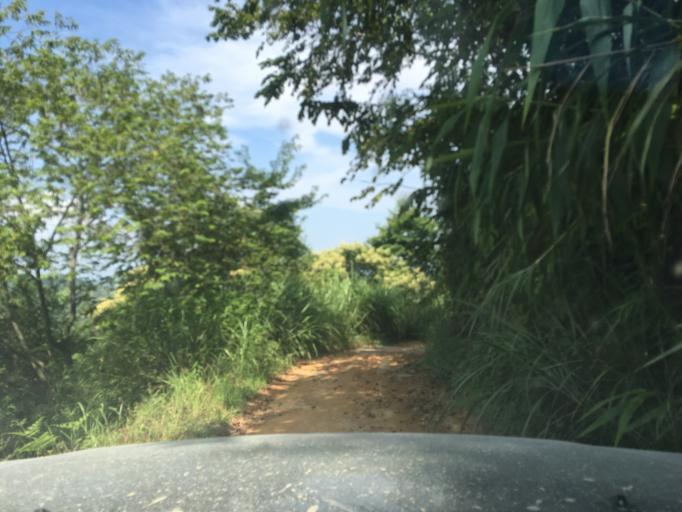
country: CN
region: Guangxi Zhuangzu Zizhiqu
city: Xinzhou
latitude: 25.0456
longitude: 105.8640
